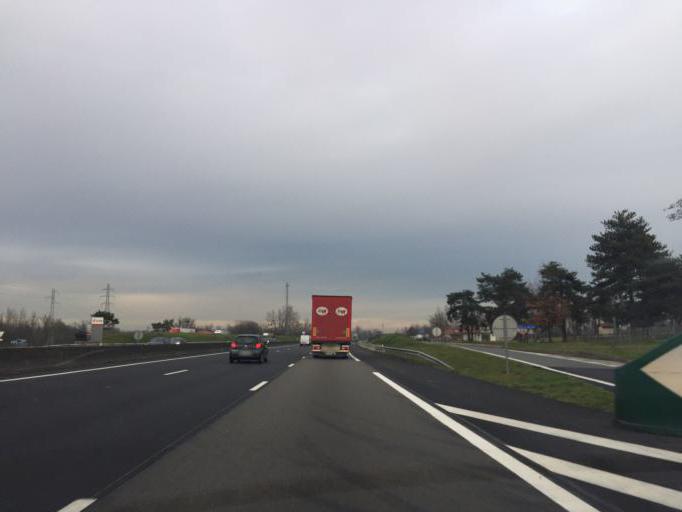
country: FR
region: Rhone-Alpes
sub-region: Departement du Rhone
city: Saint-Georges-de-Reneins
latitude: 46.0389
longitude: 4.7264
